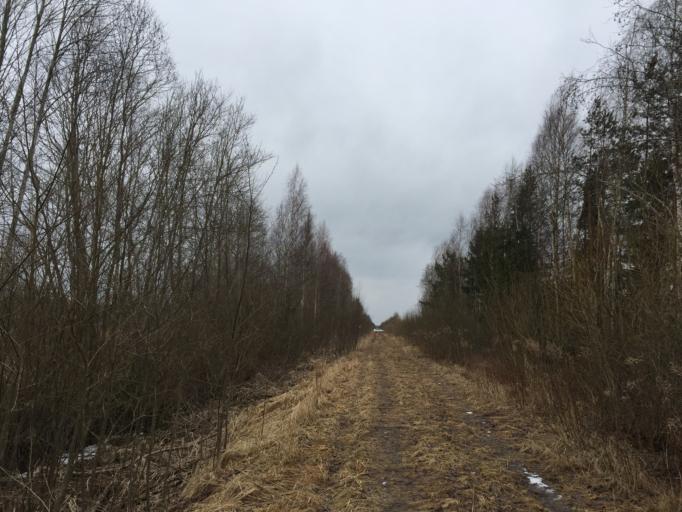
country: LV
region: Lielvarde
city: Lielvarde
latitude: 56.7592
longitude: 24.8179
